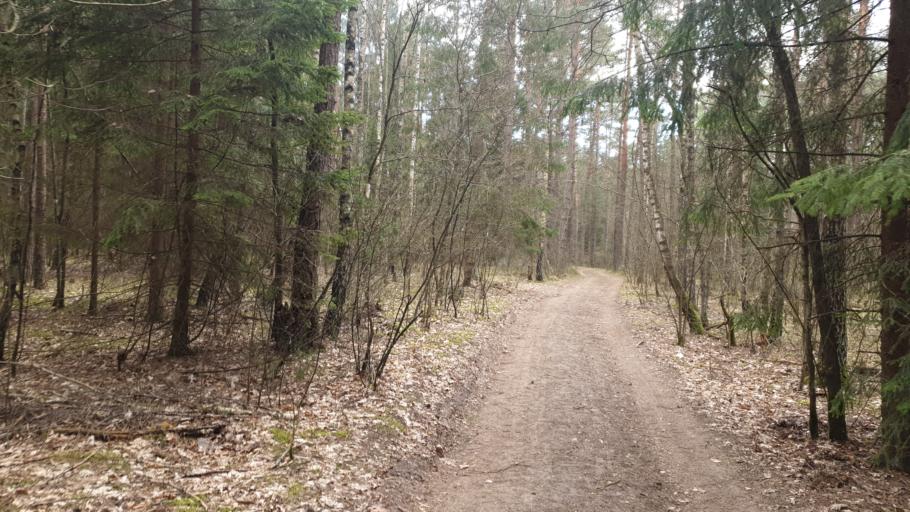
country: LT
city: Grigiskes
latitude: 54.7271
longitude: 25.0320
